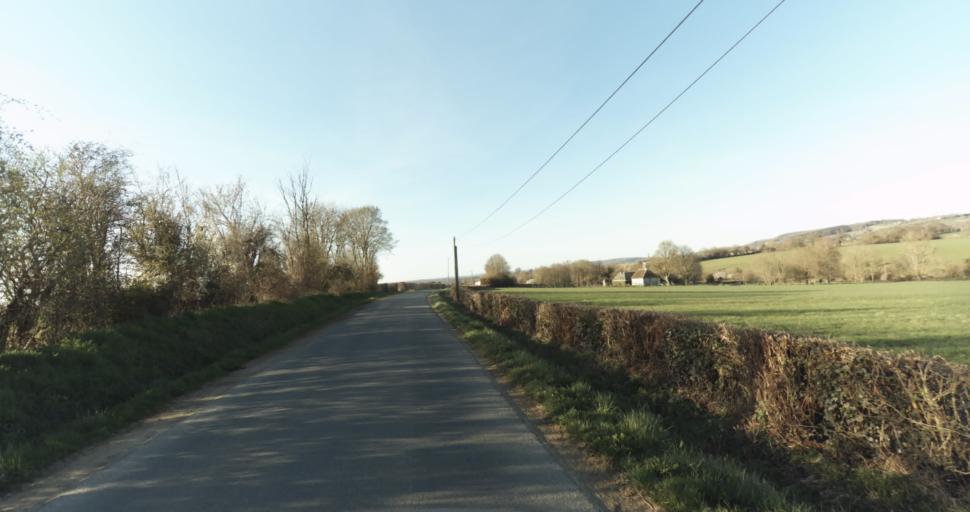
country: FR
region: Lower Normandy
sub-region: Departement de l'Orne
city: Trun
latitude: 48.9105
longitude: 0.0333
